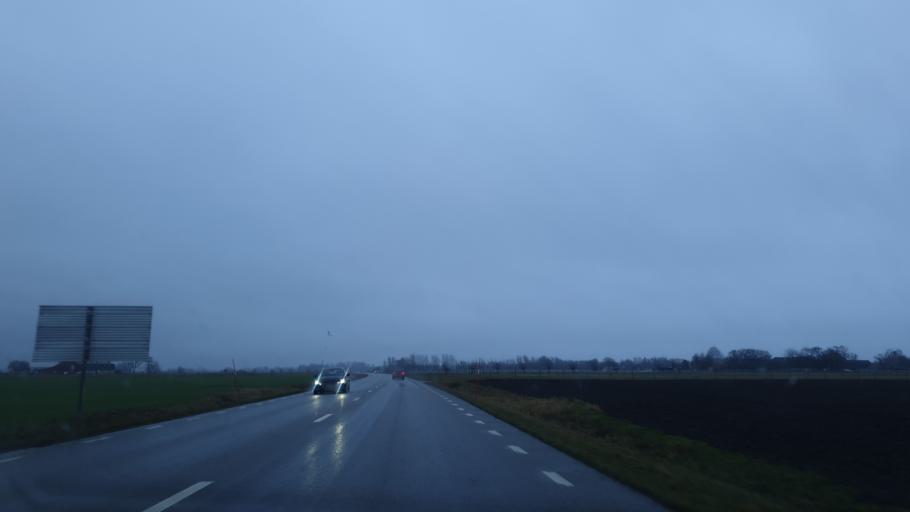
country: SE
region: Skane
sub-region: Trelleborgs Kommun
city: Trelleborg
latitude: 55.3590
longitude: 13.2424
